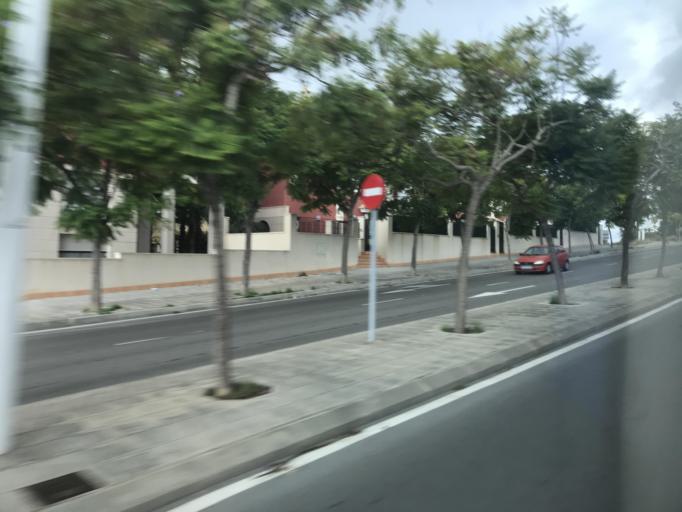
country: ES
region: Valencia
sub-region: Provincia de Alicante
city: Santa Pola
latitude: 38.2009
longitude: -0.5617
